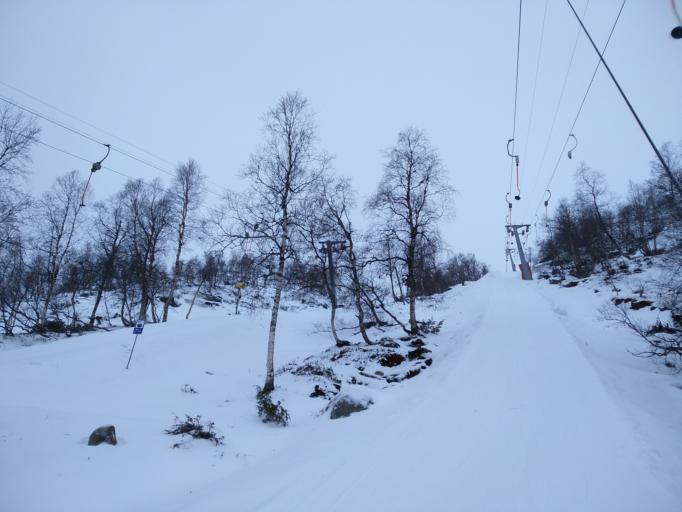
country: NO
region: Vest-Agder
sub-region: Sirdal
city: Tonstad
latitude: 59.0230
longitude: 6.9178
